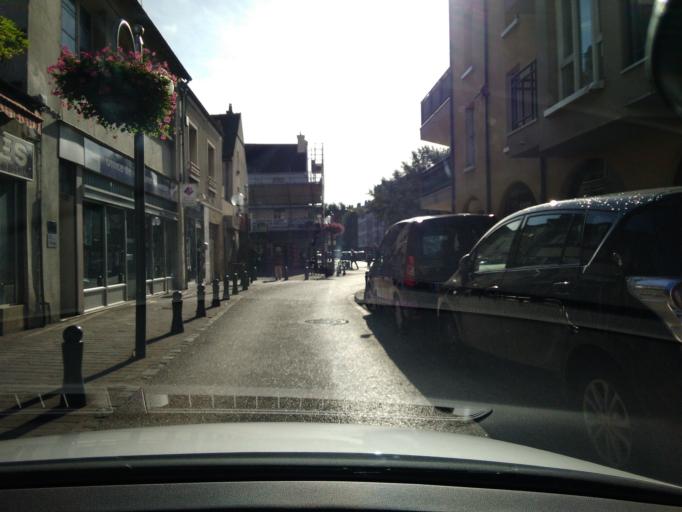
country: FR
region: Ile-de-France
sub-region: Departement de l'Essonne
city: Massy
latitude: 48.7298
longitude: 2.2752
